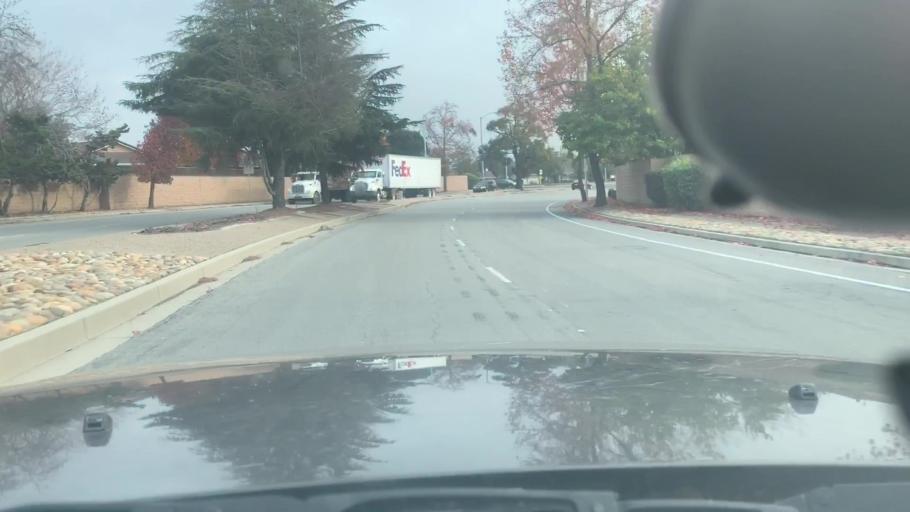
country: US
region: California
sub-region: Alameda County
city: Newark
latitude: 37.5335
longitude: -122.0242
